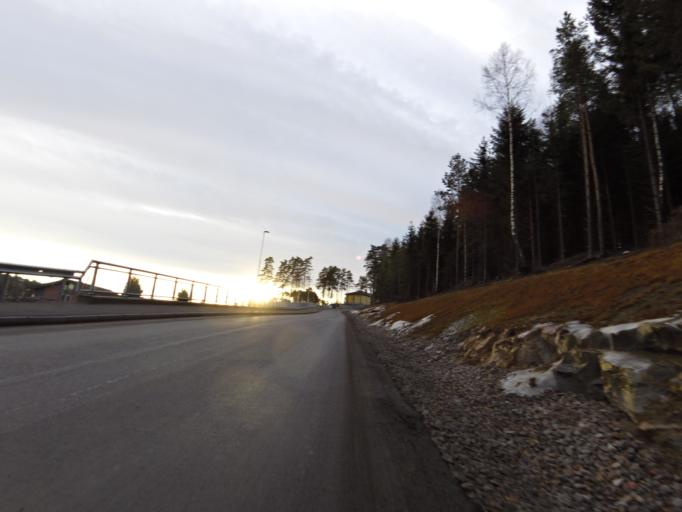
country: NO
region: Ostfold
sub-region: Fredrikstad
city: Fredrikstad
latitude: 59.2289
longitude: 10.9549
